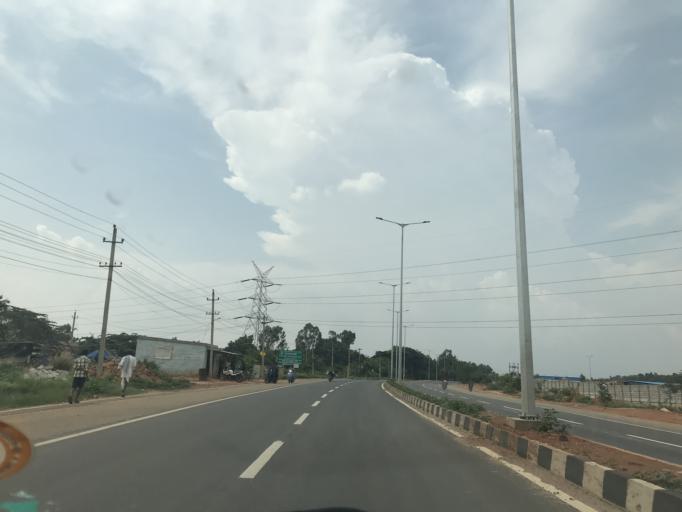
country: IN
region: Karnataka
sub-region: Bangalore Urban
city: Yelahanka
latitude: 13.1446
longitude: 77.6732
